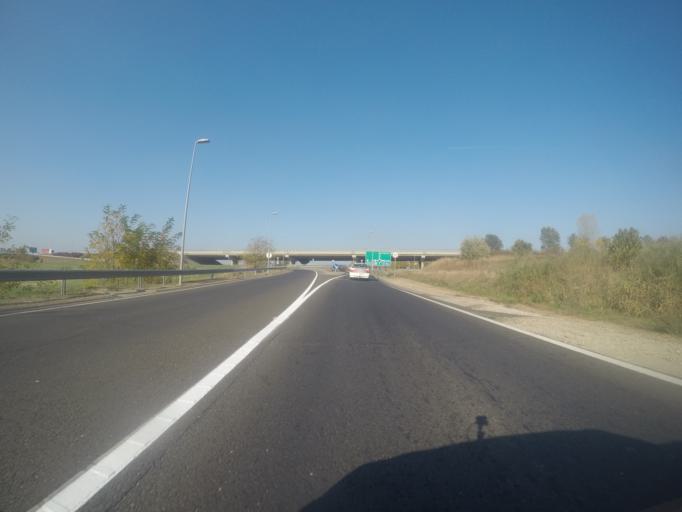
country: HU
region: Fejer
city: Baracs
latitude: 46.9094
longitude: 18.9260
